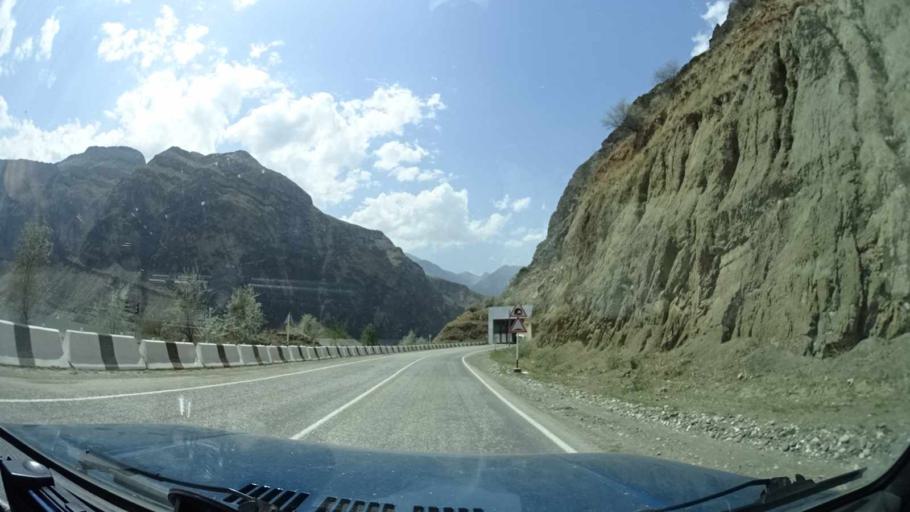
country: RU
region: Dagestan
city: Shamil'kala
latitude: 42.6948
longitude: 46.8503
